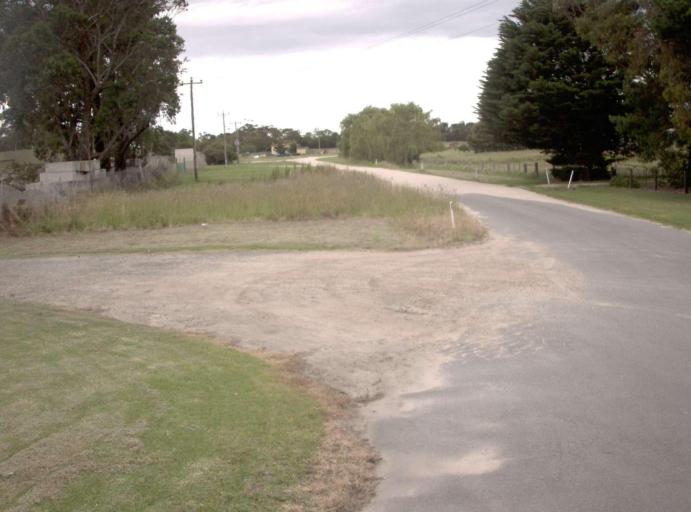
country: AU
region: Victoria
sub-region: Wellington
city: Sale
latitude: -38.1157
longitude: 147.0683
